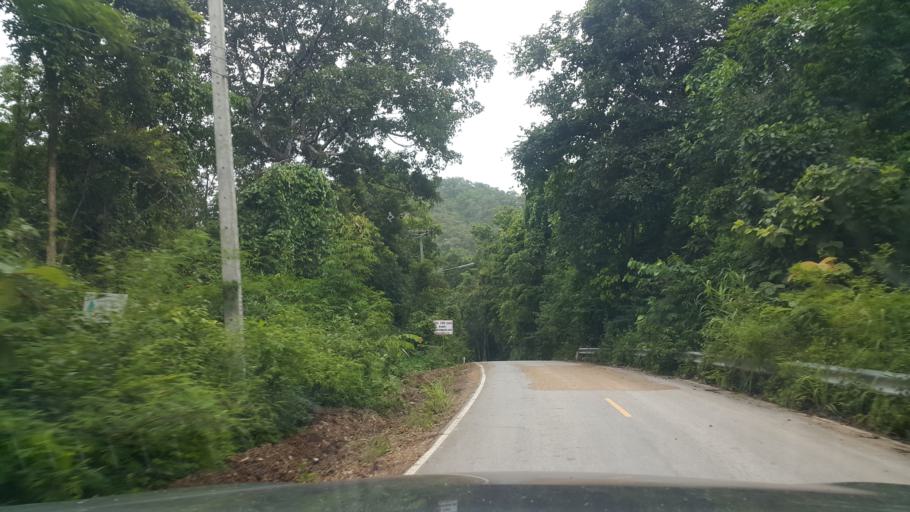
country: TH
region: Chiang Mai
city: San Sai
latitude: 18.9713
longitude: 99.1250
